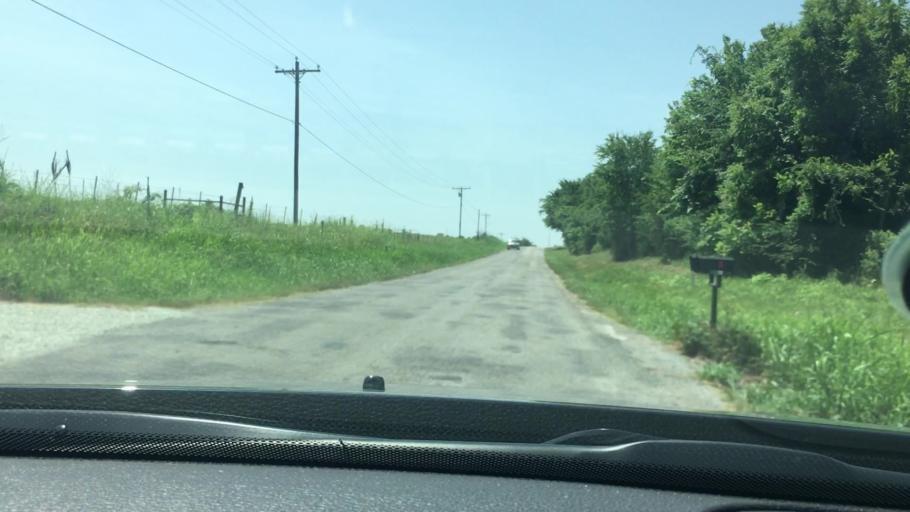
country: US
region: Oklahoma
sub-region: Pontotoc County
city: Byng
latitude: 34.8328
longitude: -96.6698
